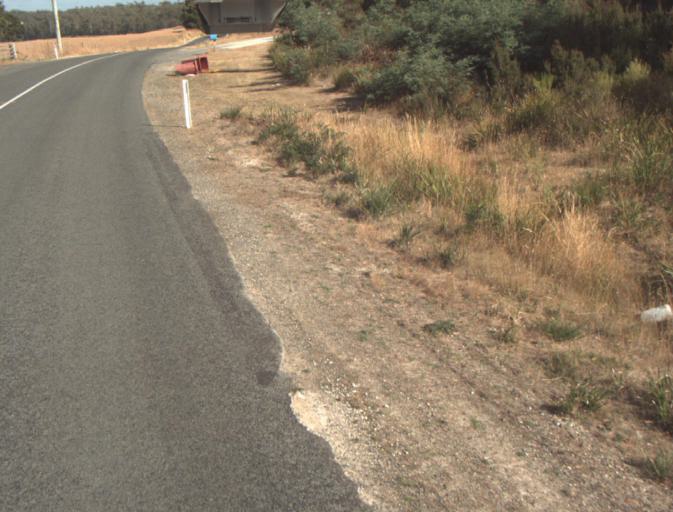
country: AU
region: Tasmania
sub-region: Dorset
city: Bridport
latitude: -41.1329
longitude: 147.2181
